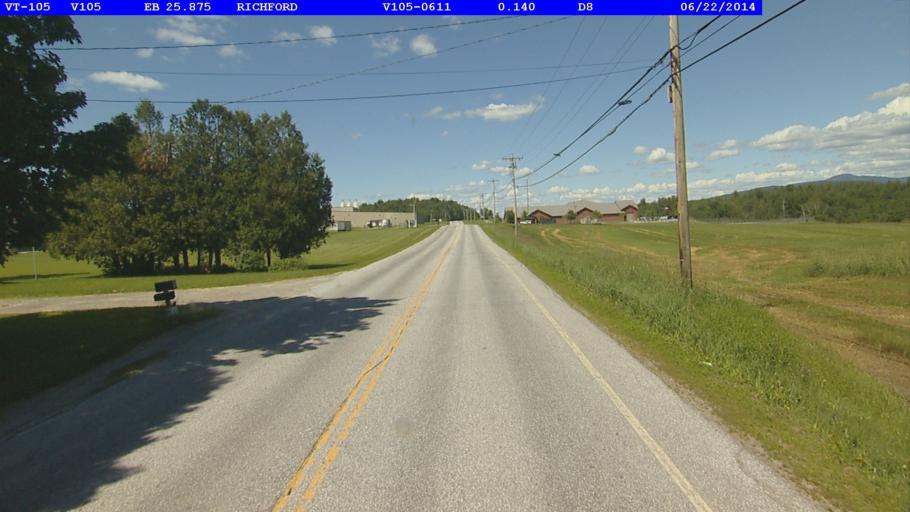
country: US
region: Vermont
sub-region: Franklin County
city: Richford
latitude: 44.9733
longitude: -72.6885
